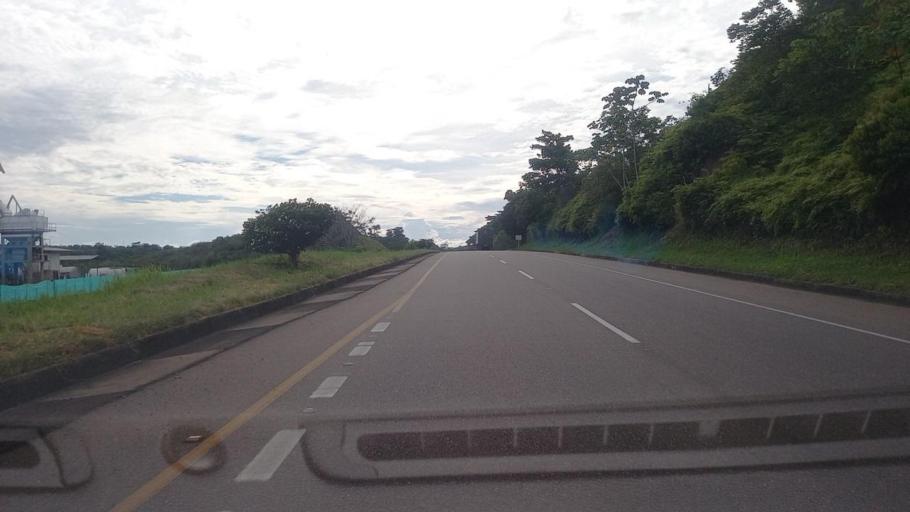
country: CO
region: Antioquia
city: Puerto Berrio
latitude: 6.3762
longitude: -74.4021
